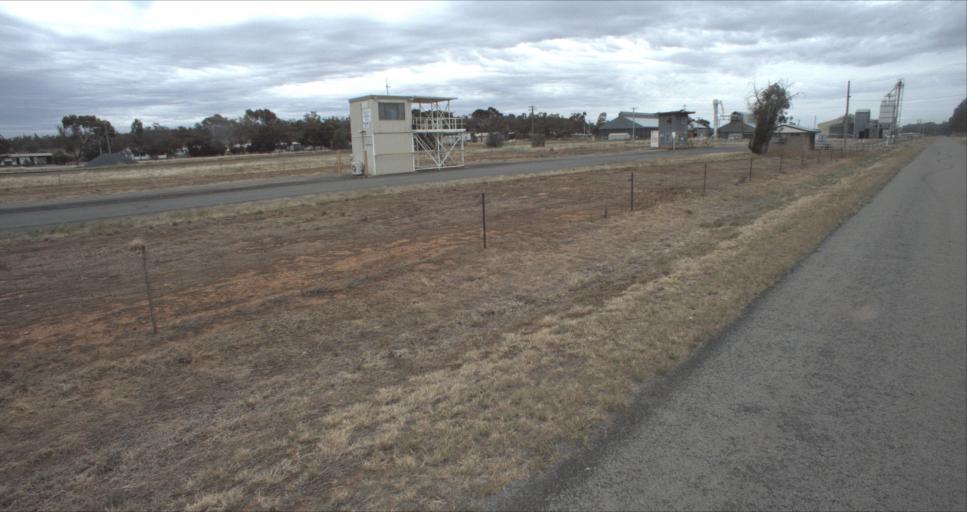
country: AU
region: New South Wales
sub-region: Leeton
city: Leeton
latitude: -34.4278
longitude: 146.3010
